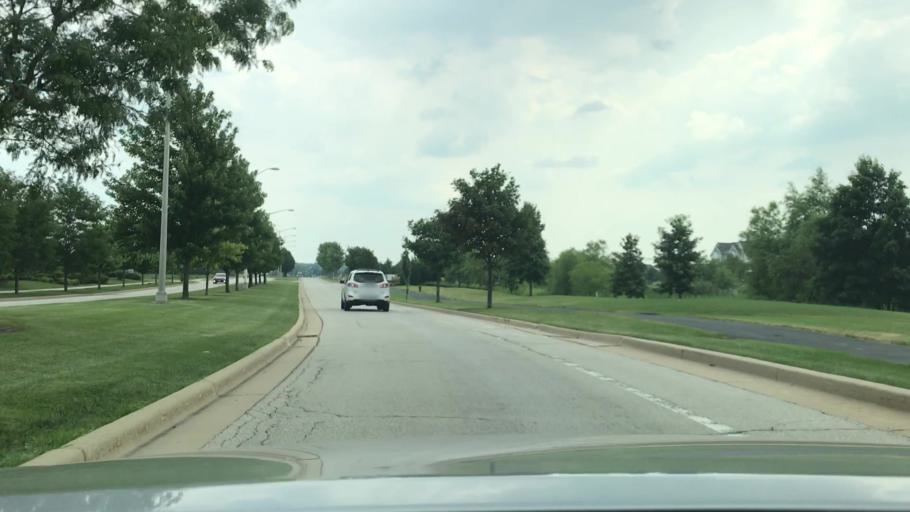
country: US
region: Illinois
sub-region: Will County
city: Plainfield
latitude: 41.6152
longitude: -88.2160
